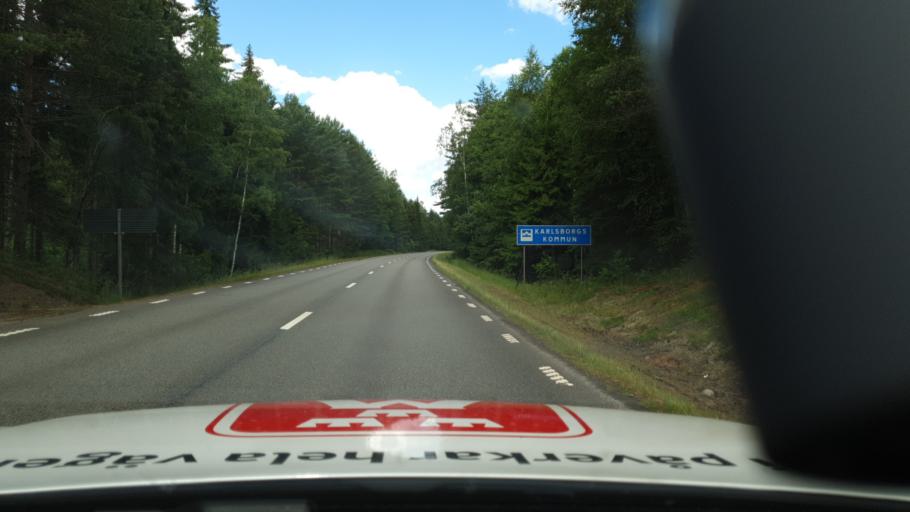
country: SE
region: Vaestra Goetaland
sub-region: Karlsborgs Kommun
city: Molltorp
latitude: 58.4043
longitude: 14.3623
